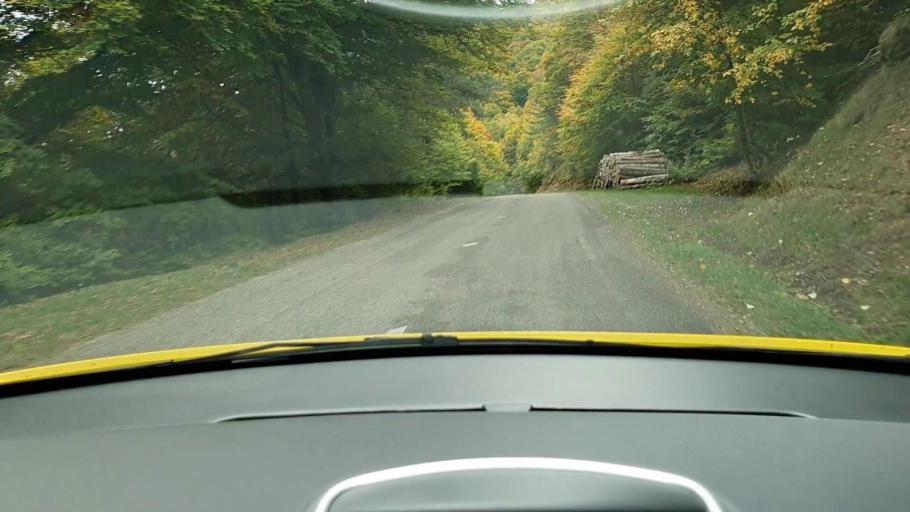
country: FR
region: Languedoc-Roussillon
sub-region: Departement de la Lozere
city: Meyrueis
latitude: 44.0911
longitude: 3.4431
